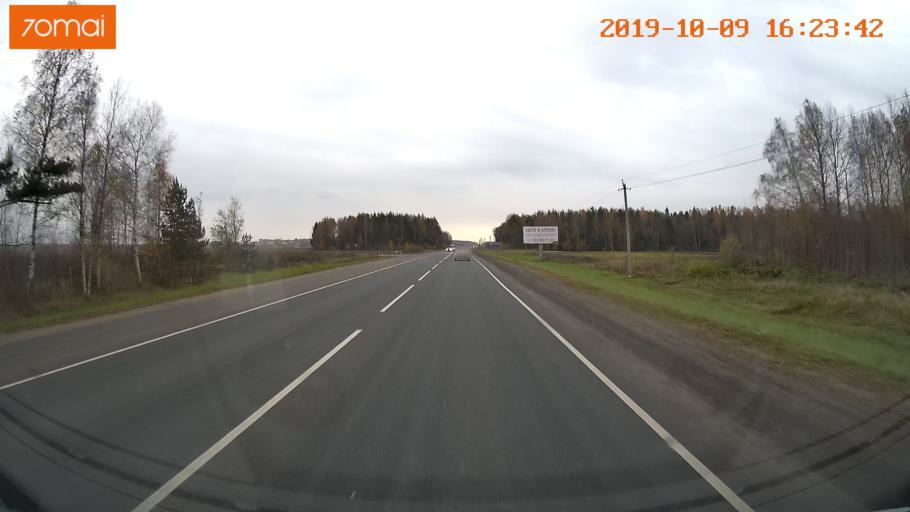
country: RU
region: Kostroma
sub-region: Kostromskoy Rayon
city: Kostroma
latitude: 57.6605
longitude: 40.9028
